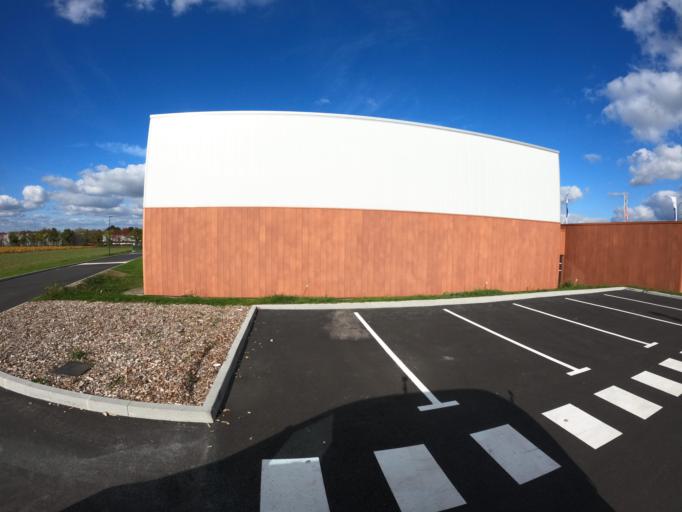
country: FR
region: Pays de la Loire
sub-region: Departement de la Loire-Atlantique
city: Aigrefeuille-sur-Maine
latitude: 47.0741
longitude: -1.4153
